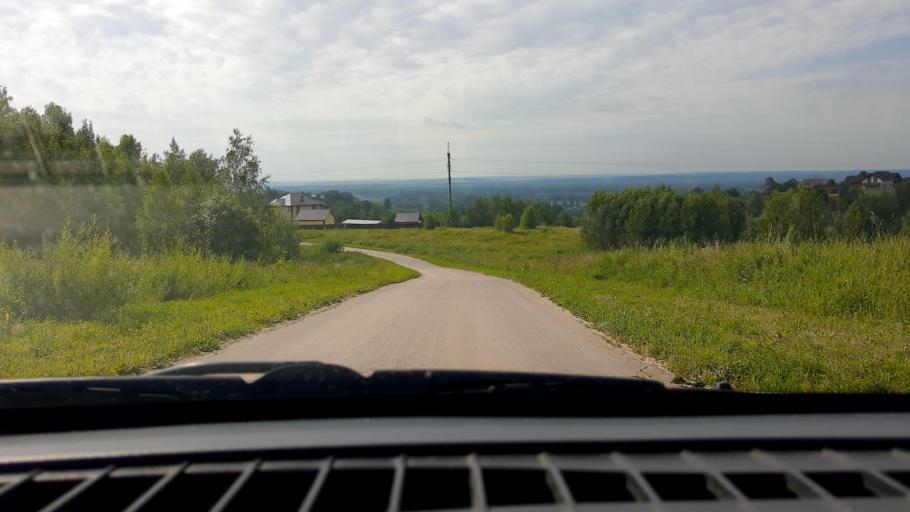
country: RU
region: Nizjnij Novgorod
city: Kstovo
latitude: 56.1112
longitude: 44.3109
